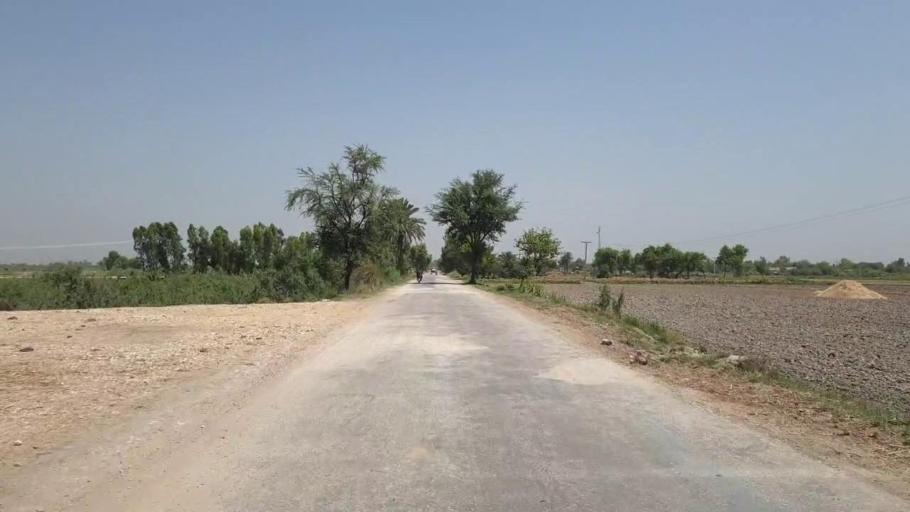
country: PK
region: Sindh
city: Adilpur
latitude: 27.8864
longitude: 69.2881
